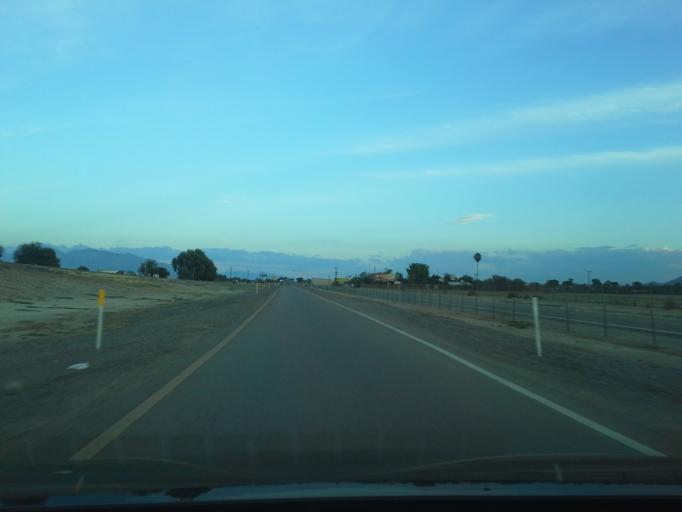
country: US
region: Arizona
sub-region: Pima County
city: Marana
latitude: 32.4604
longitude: -111.2153
